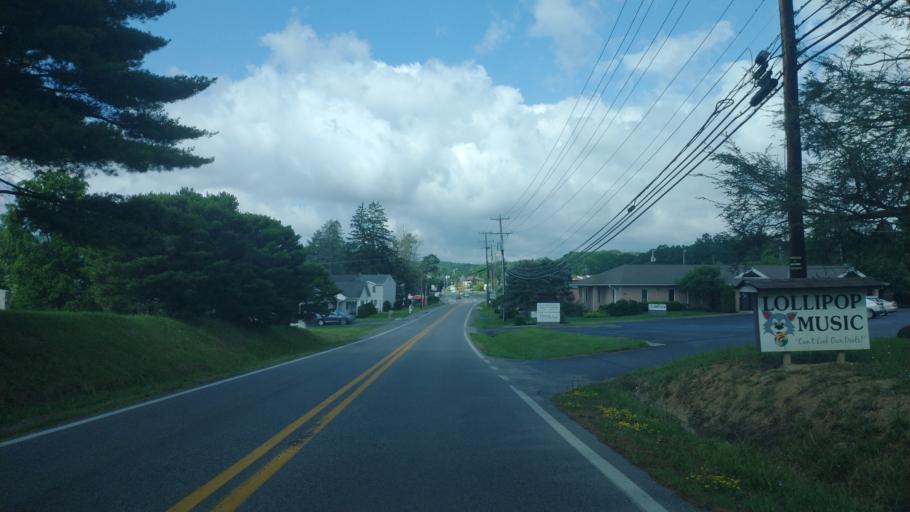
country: US
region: West Virginia
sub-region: Mercer County
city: Princeton
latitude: 37.3669
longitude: -81.1119
